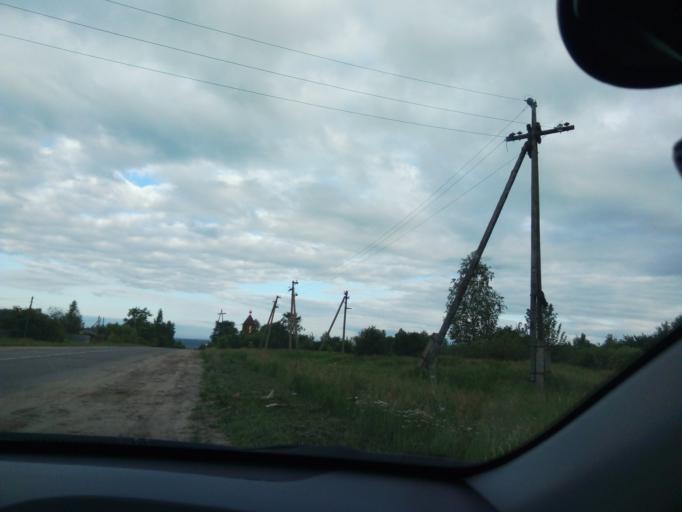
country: RU
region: Rjazan
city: Yermish'
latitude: 54.5769
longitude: 42.1223
